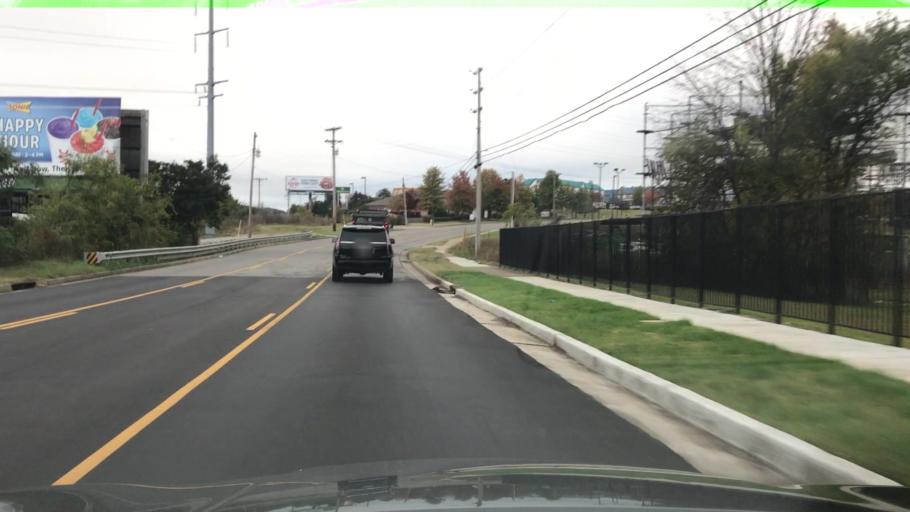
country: US
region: Tennessee
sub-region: Williamson County
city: Franklin
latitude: 35.9073
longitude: -86.8243
